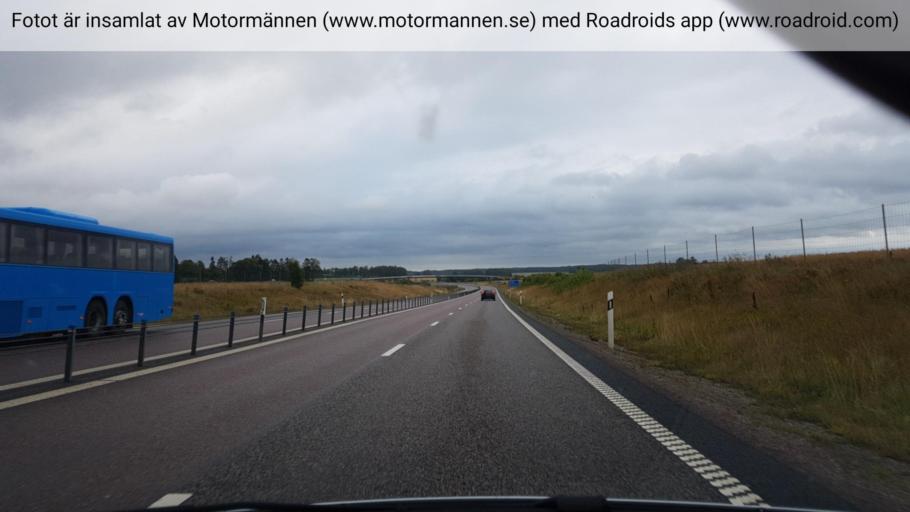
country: SE
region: Vaestra Goetaland
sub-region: Skovde Kommun
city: Skultorp
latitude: 58.3205
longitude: 13.8240
